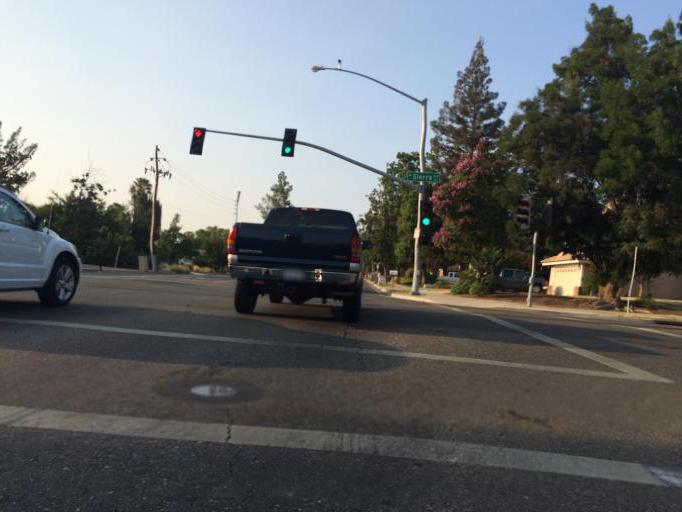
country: US
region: California
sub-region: Fresno County
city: Fresno
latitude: 36.8299
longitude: -119.8172
